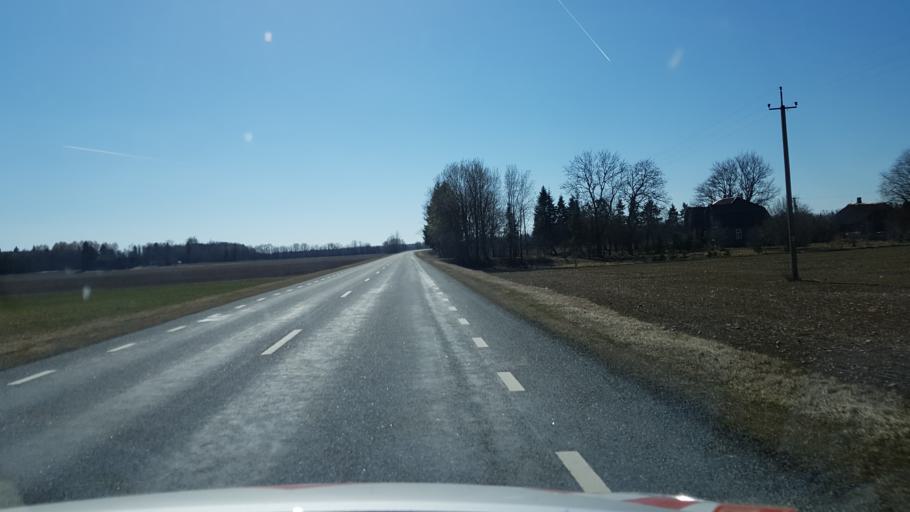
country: EE
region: Jaervamaa
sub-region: Jaerva-Jaani vald
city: Jarva-Jaani
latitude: 59.0755
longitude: 25.9547
